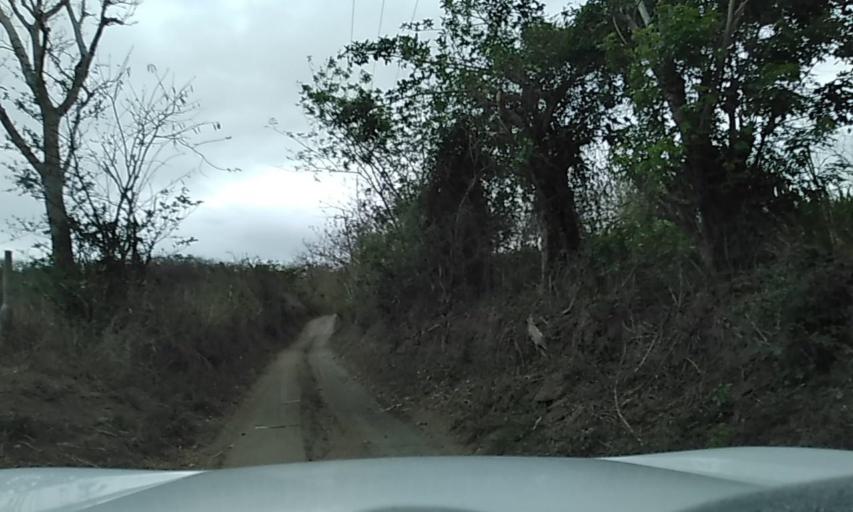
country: MX
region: Veracruz
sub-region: Veracruz
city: Delfino Victoria (Santa Fe)
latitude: 19.2748
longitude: -96.3110
